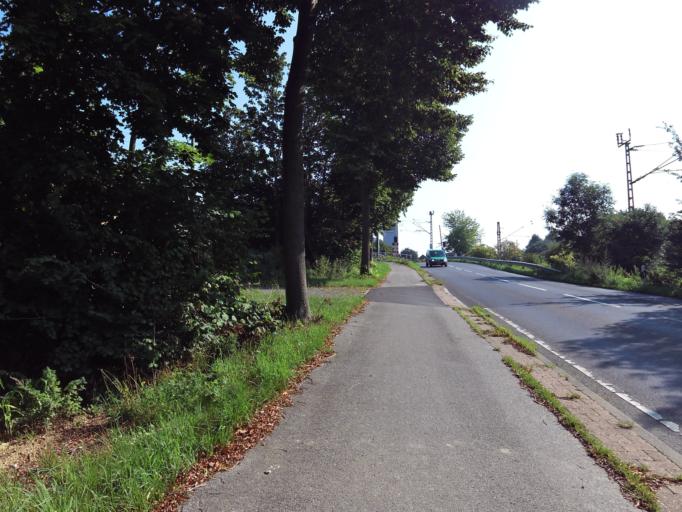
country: DE
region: North Rhine-Westphalia
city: Huckelhoven
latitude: 50.9955
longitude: 6.2013
